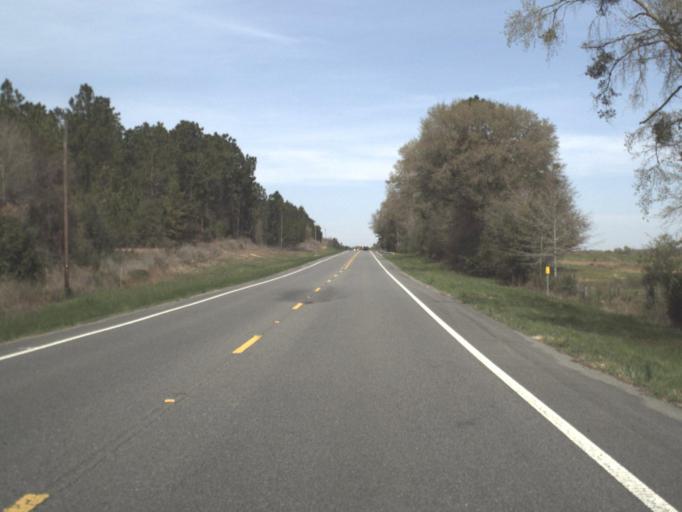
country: US
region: Florida
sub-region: Walton County
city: DeFuniak Springs
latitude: 30.8096
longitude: -85.9583
